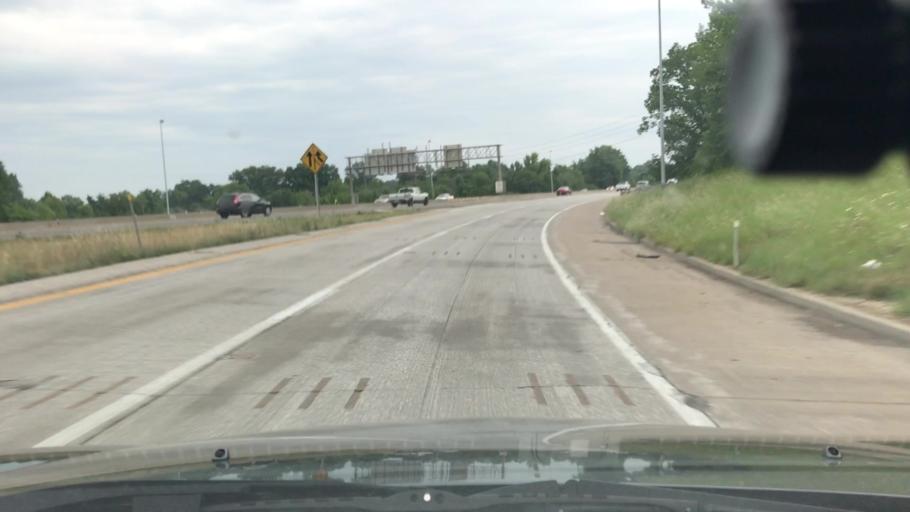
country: US
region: Missouri
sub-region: Saint Louis County
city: Creve Coeur
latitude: 38.6417
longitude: -90.4489
